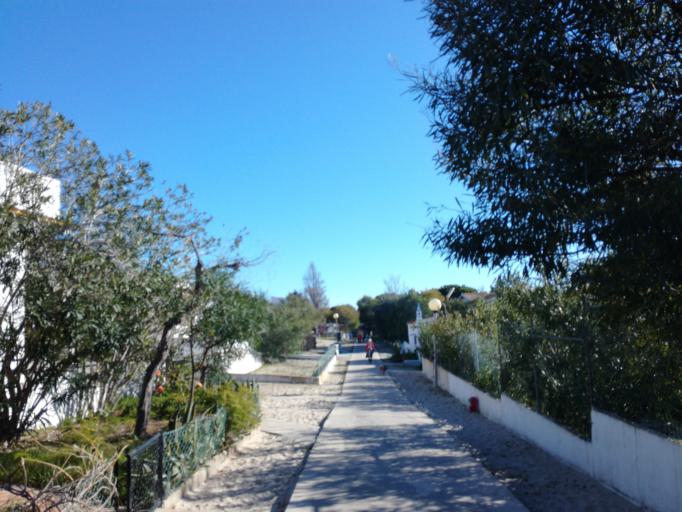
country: PT
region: Faro
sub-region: Olhao
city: Olhao
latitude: 37.0206
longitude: -7.8047
